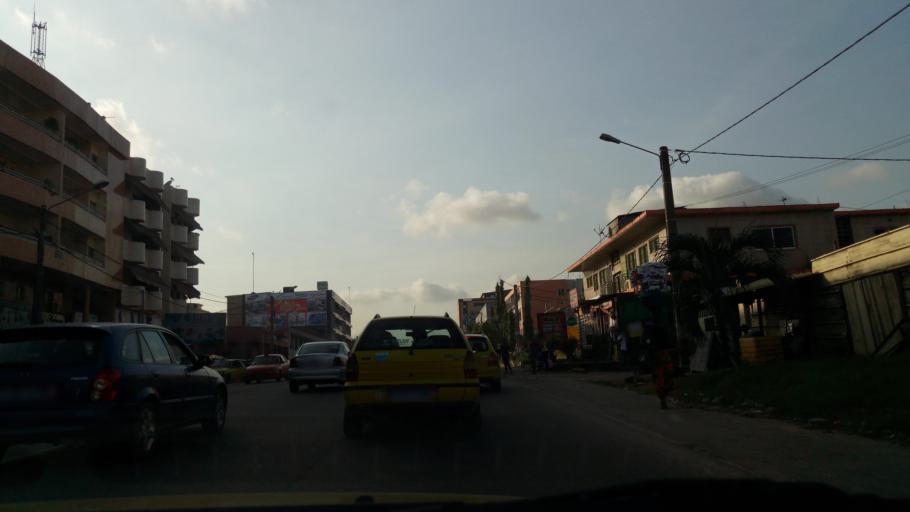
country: CI
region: Lagunes
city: Abobo
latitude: 5.3948
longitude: -3.9767
